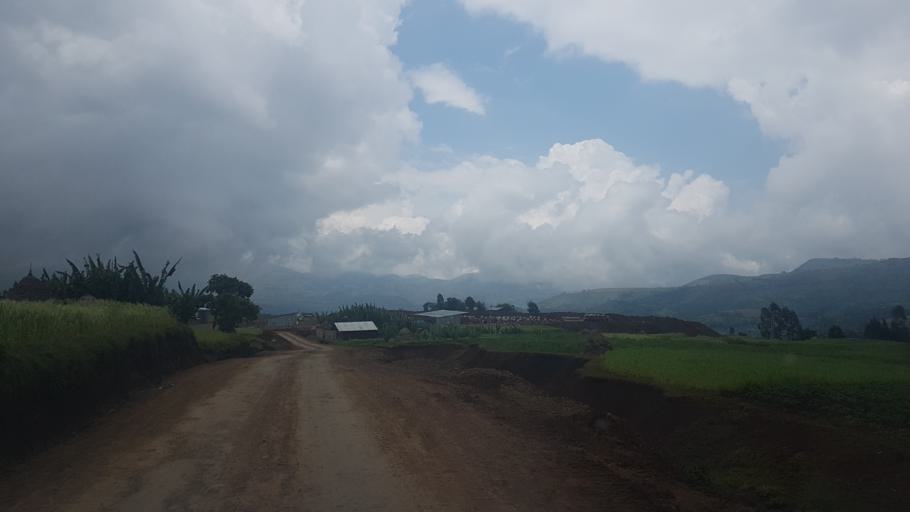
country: ET
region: Southern Nations, Nationalities, and People's Region
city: Arba Minch'
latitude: 6.3259
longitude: 37.5441
